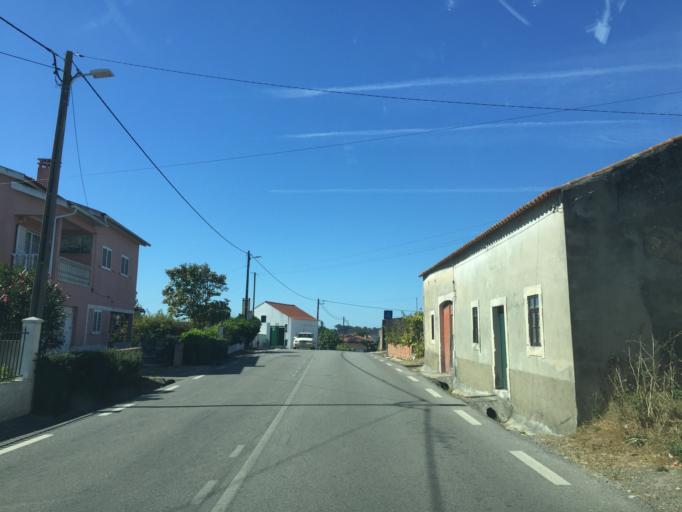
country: PT
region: Coimbra
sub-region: Mira
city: Mira
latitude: 40.3187
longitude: -8.7668
